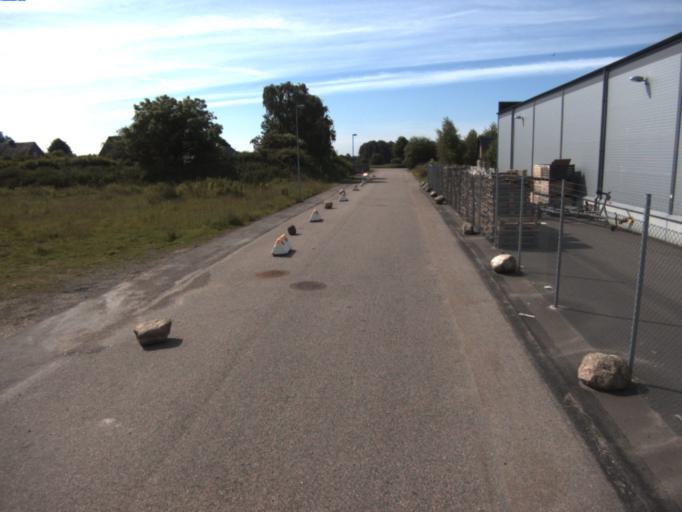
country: SE
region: Skane
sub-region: Helsingborg
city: Barslov
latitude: 56.0322
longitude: 12.7822
